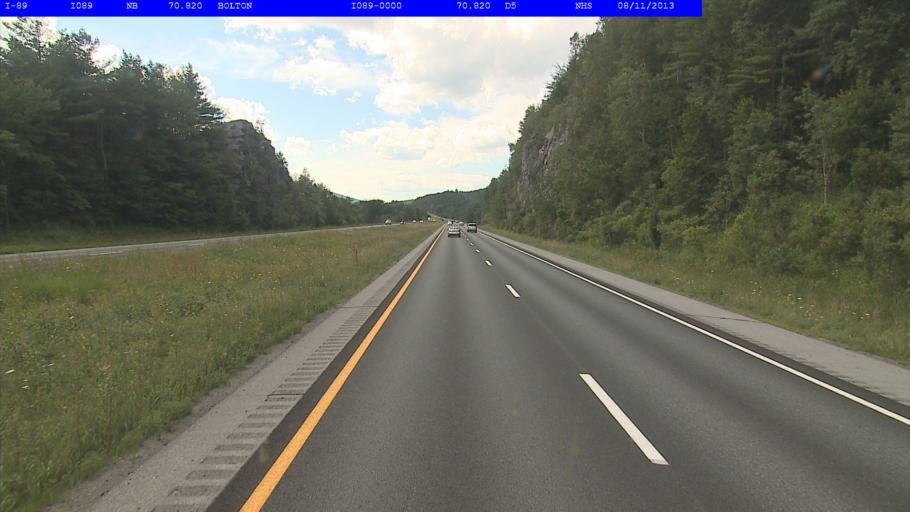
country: US
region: Vermont
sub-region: Washington County
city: Waterbury
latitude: 44.3746
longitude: -72.8833
